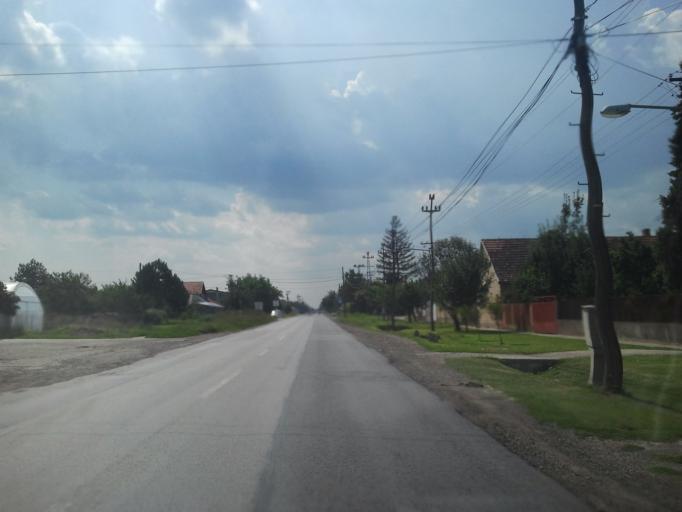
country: RS
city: Glozan
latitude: 45.2410
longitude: 19.6318
